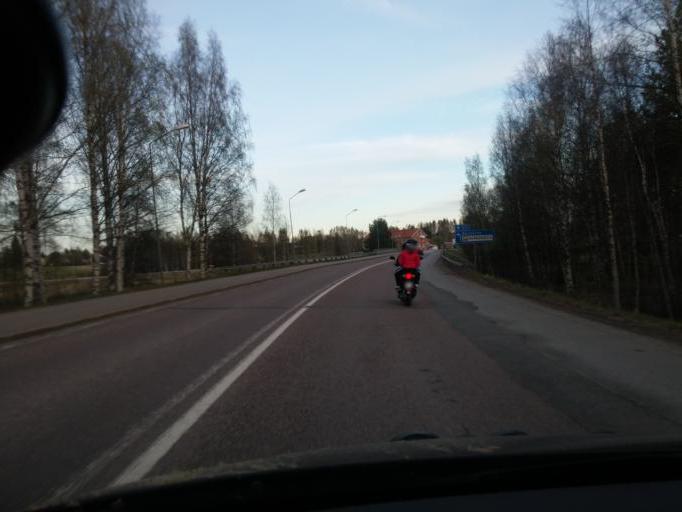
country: SE
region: Gaevleborg
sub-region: Ljusdals Kommun
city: Ljusdal
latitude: 61.8350
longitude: 16.0666
